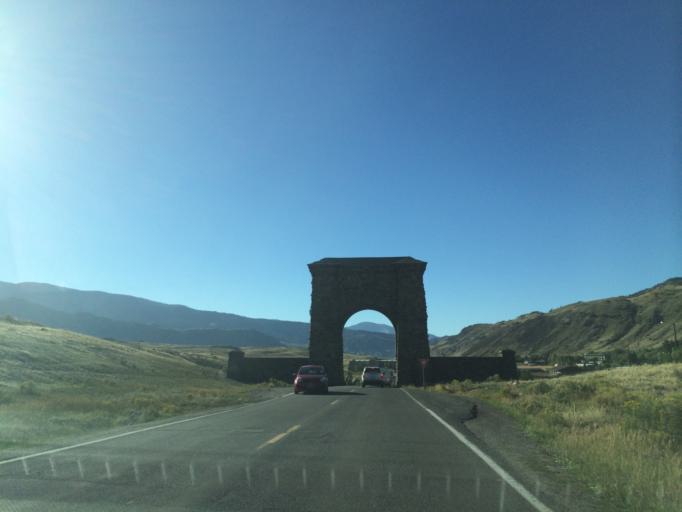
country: US
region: Montana
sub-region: Gallatin County
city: West Yellowstone
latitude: 45.0291
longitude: -110.7080
